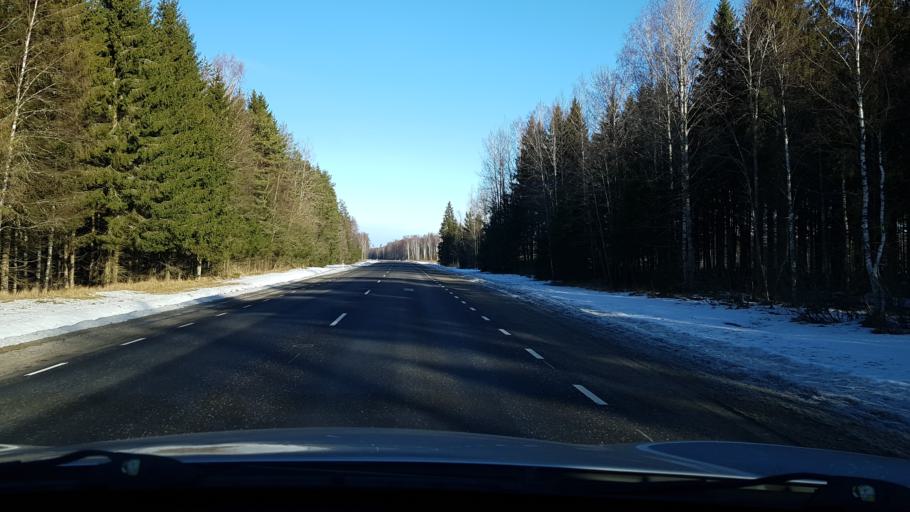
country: EE
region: Viljandimaa
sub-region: Vohma linn
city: Vohma
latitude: 58.5928
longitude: 25.5719
